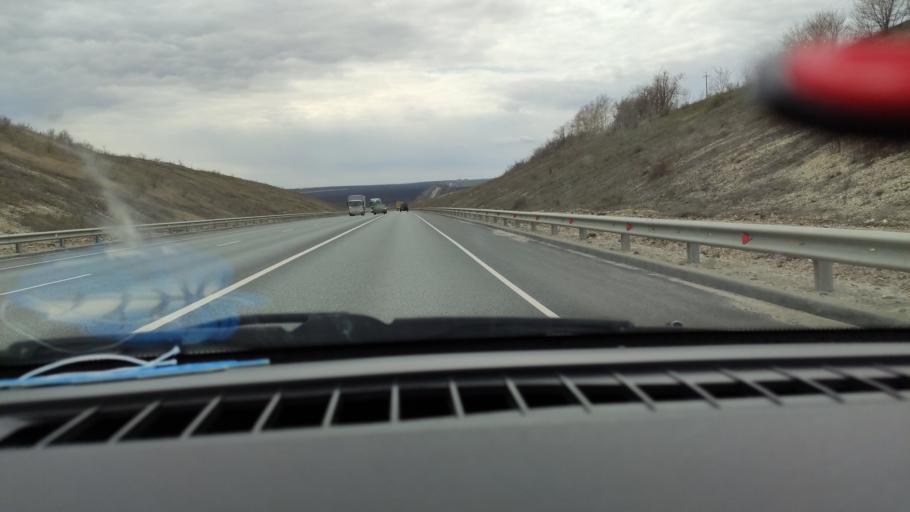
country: RU
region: Saratov
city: Yelshanka
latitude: 51.8821
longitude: 46.5117
